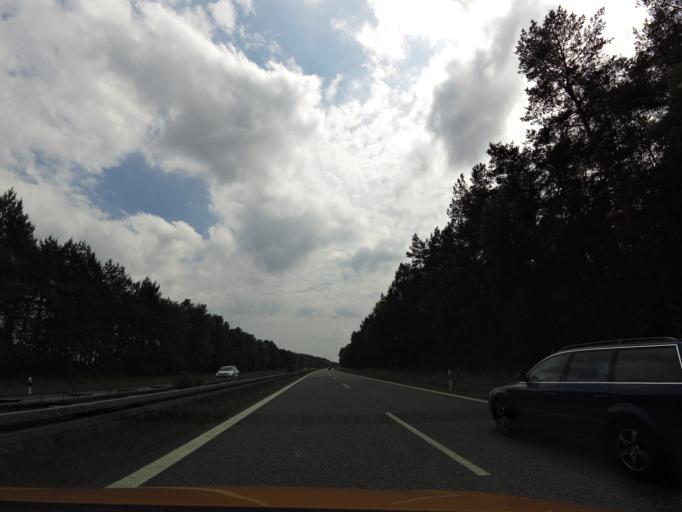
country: DE
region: Mecklenburg-Vorpommern
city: Mirow
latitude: 53.5098
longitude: 11.4716
